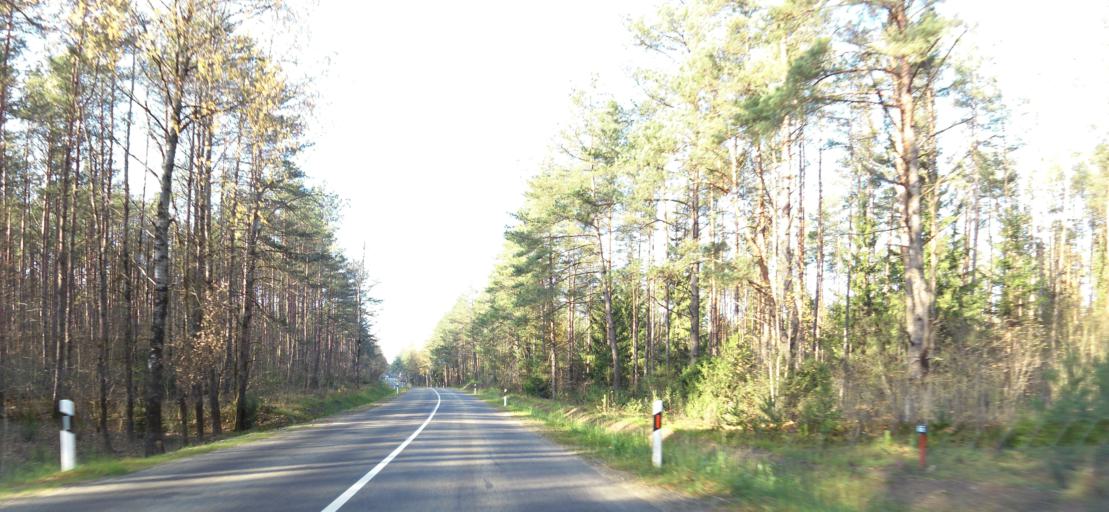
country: LT
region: Vilnius County
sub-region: Trakai
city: Rudiskes
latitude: 54.5109
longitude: 24.9218
